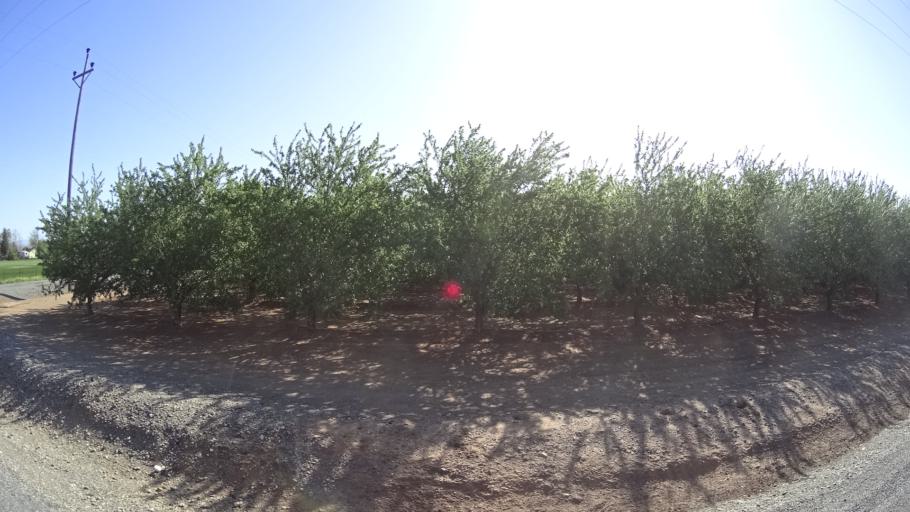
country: US
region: California
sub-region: Glenn County
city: Hamilton City
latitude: 39.7754
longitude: -122.0666
